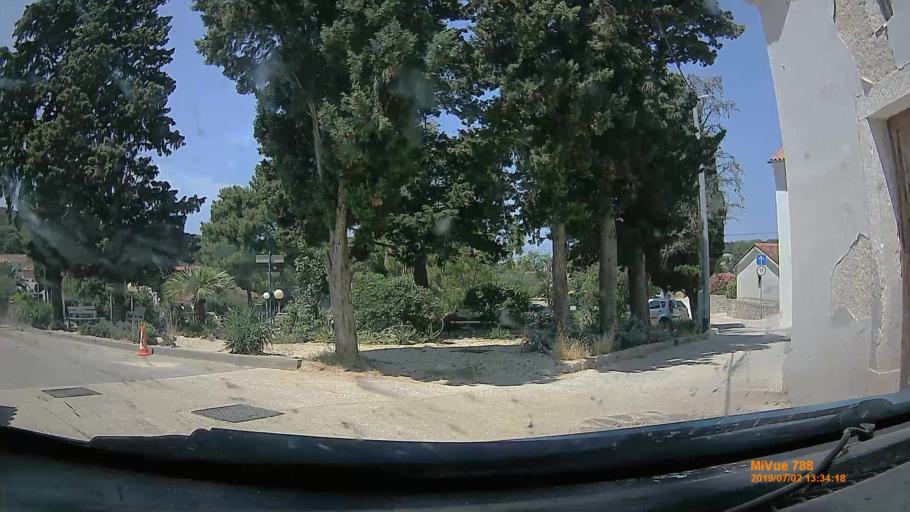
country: HR
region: Primorsko-Goranska
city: Mali Losinj
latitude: 44.5169
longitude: 14.5048
